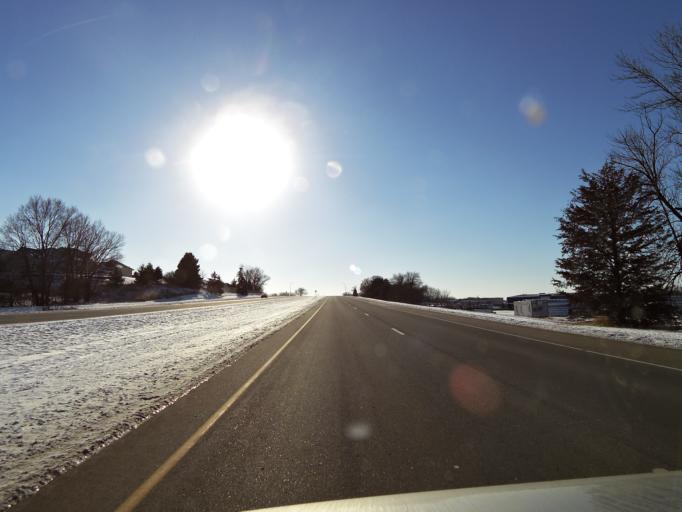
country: US
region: Minnesota
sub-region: Scott County
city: Shakopee
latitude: 44.7898
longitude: -93.5516
